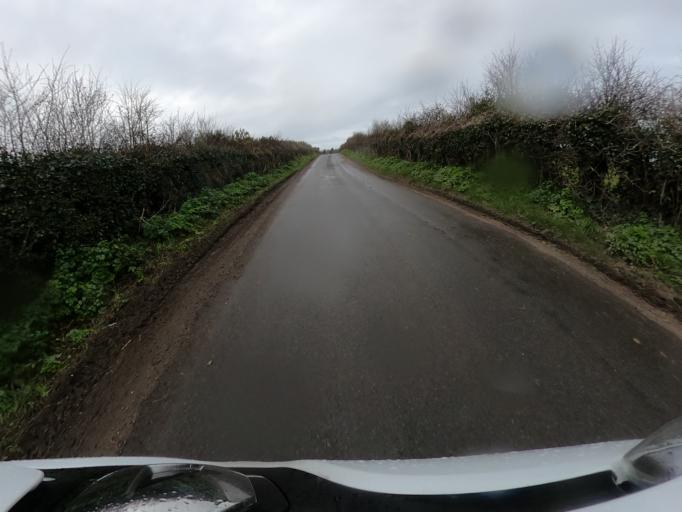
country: IM
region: Ramsey
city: Ramsey
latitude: 54.3803
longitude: -4.4602
